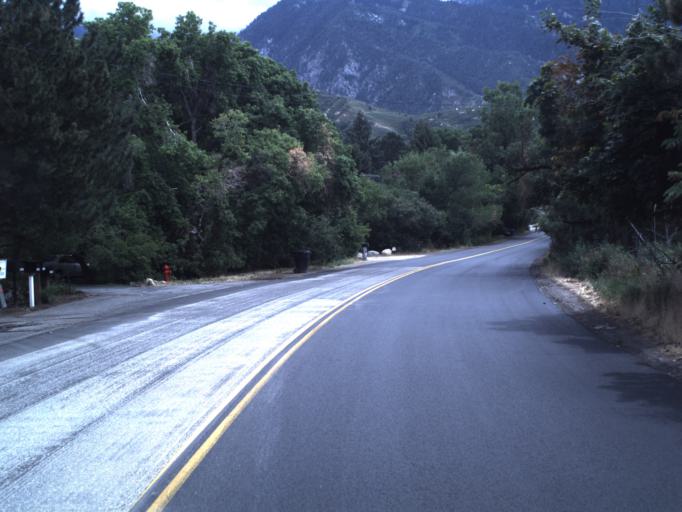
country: US
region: Utah
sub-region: Salt Lake County
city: Granite
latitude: 40.5776
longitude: -111.8024
